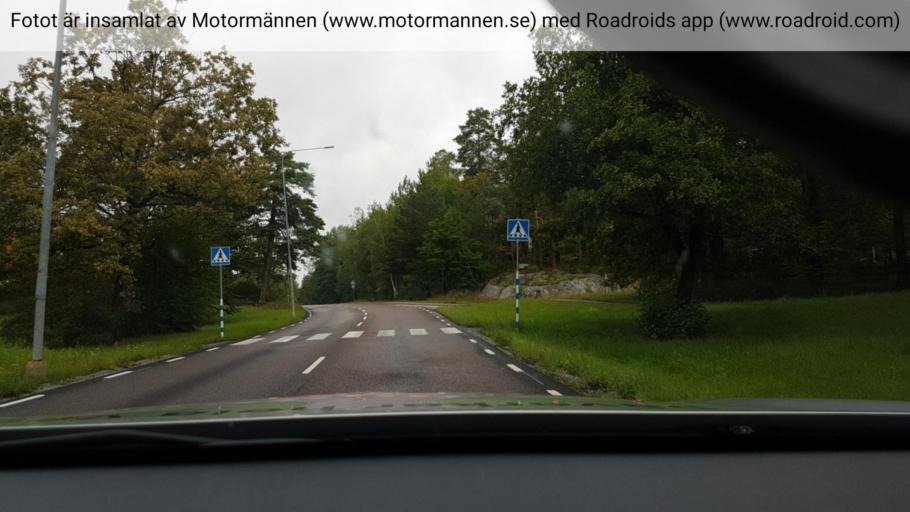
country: SE
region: Stockholm
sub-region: Lidingo
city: Brevik
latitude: 59.3493
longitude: 18.1695
